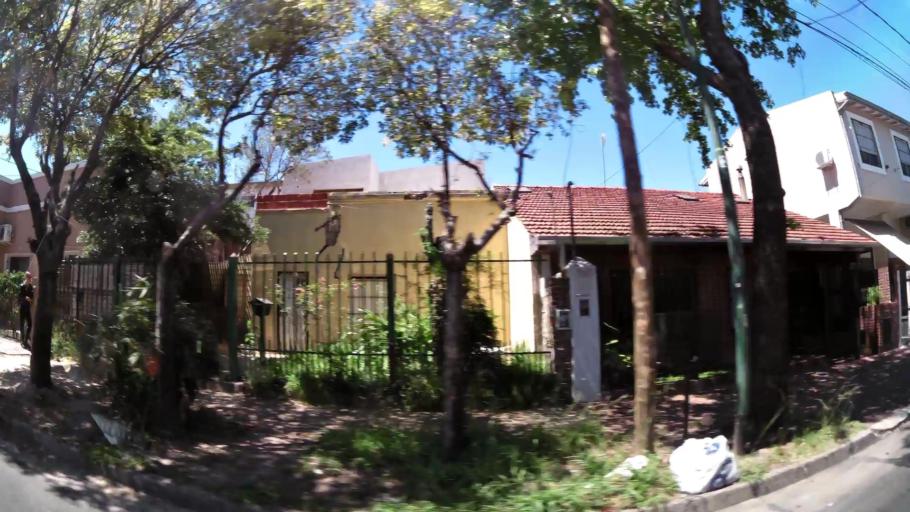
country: AR
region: Buenos Aires
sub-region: Partido de San Isidro
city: San Isidro
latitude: -34.4725
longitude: -58.5272
